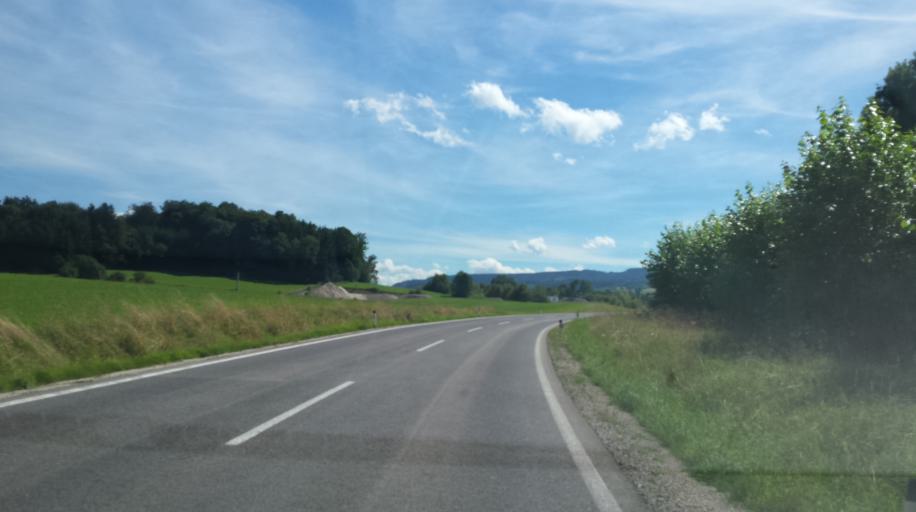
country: AT
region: Upper Austria
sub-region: Politischer Bezirk Vocklabruck
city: Sankt Georgen im Attergau
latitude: 47.9341
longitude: 13.5038
